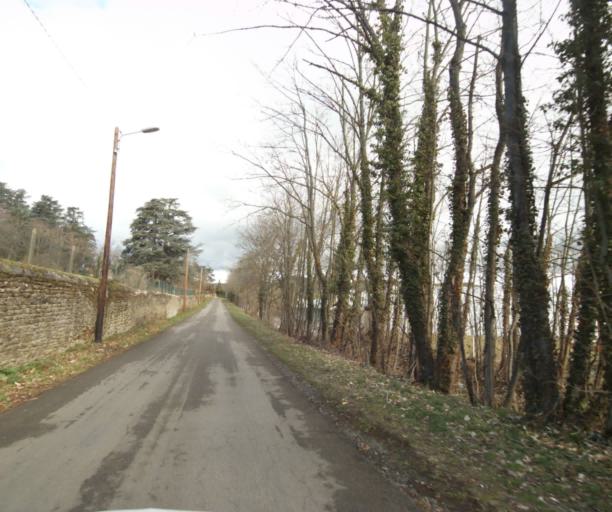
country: FR
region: Rhone-Alpes
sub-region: Departement de la Loire
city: La Talaudiere
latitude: 45.4700
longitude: 4.4213
